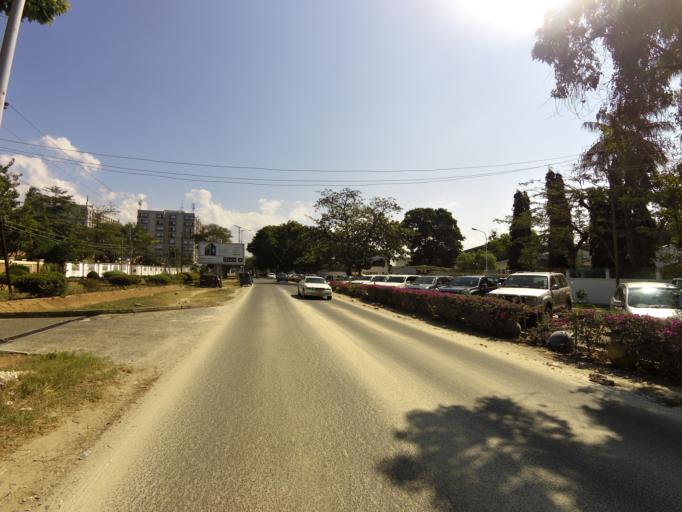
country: TZ
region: Dar es Salaam
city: Magomeni
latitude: -6.7600
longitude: 39.2789
